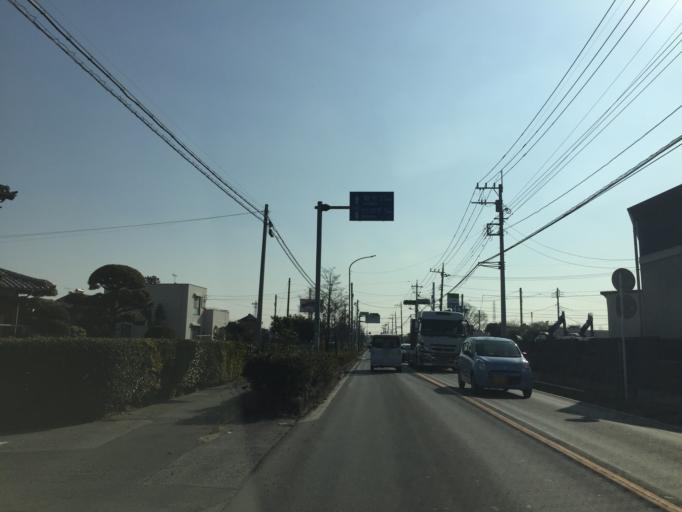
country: JP
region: Saitama
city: Shiki
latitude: 35.8363
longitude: 139.5962
